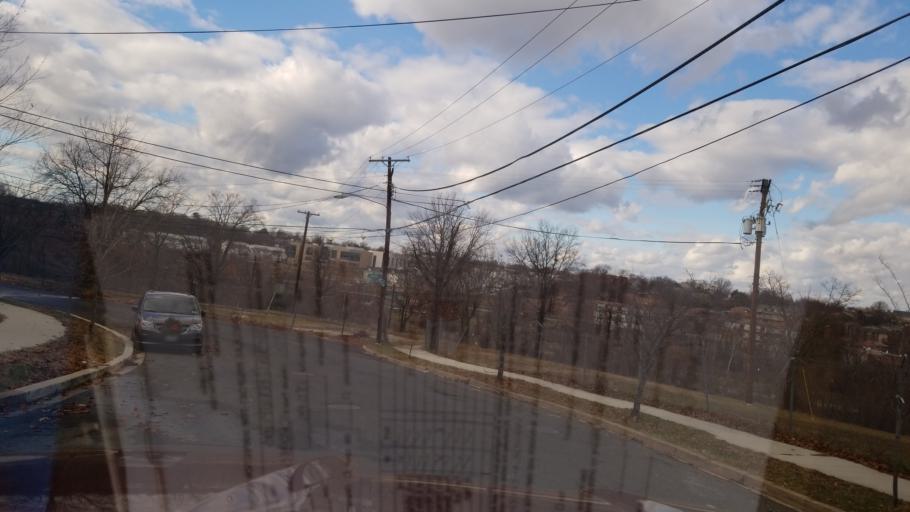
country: US
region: Maryland
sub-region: Prince George's County
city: Glassmanor
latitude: 38.8340
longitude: -76.9950
